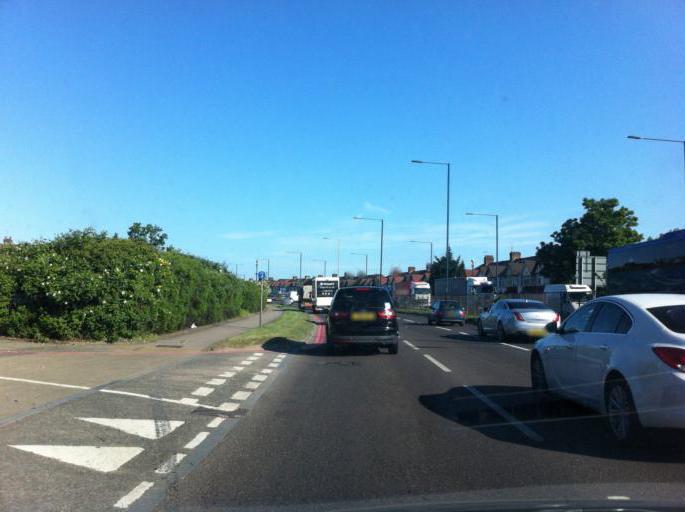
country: GB
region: England
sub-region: Greater London
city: Acton
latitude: 51.5226
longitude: -0.2645
